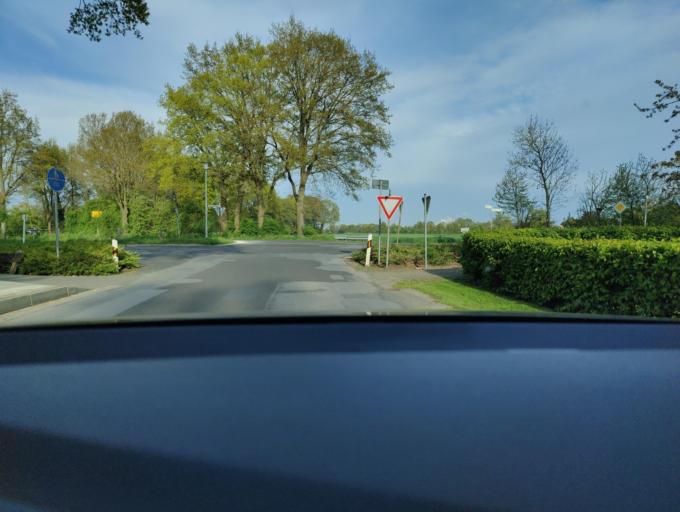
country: DE
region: Lower Saxony
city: Wietmarschen
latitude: 52.5069
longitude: 7.1389
